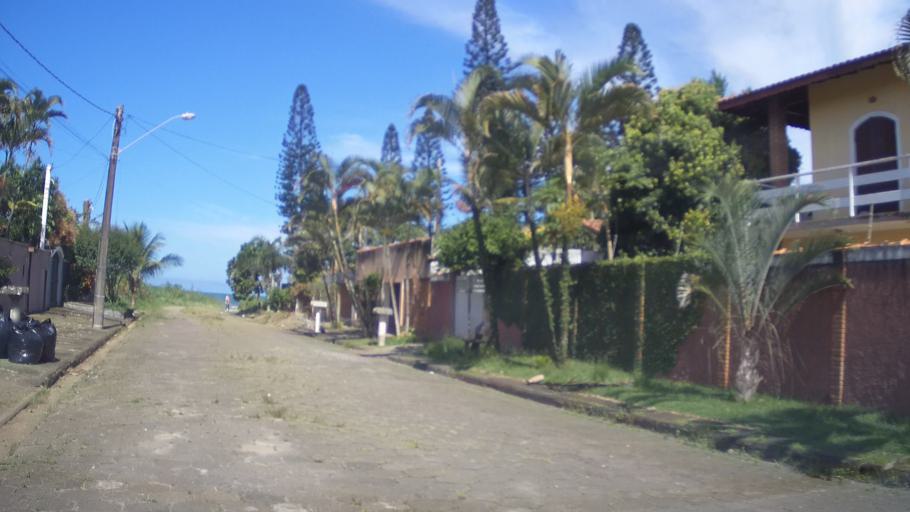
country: BR
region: Sao Paulo
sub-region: Itanhaem
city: Itanhaem
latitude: -24.1620
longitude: -46.7449
